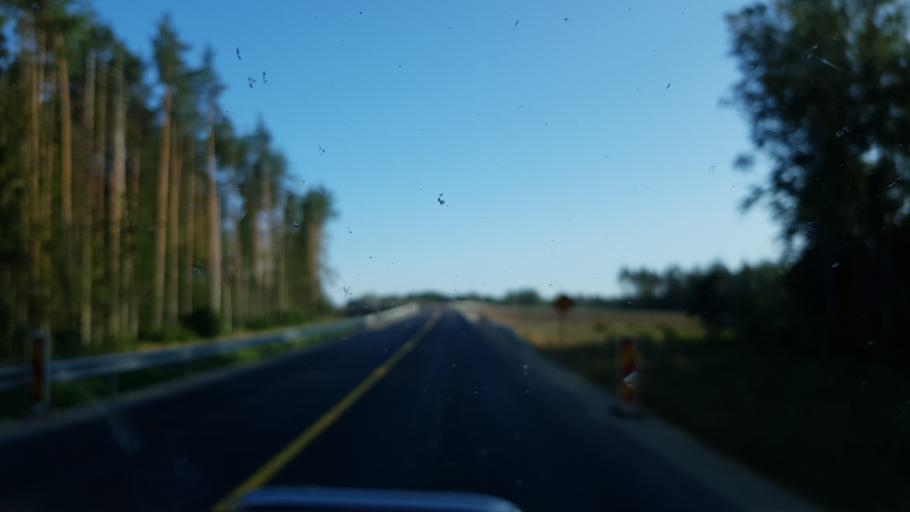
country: EE
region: Harju
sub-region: Raasiku vald
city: Raasiku
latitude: 59.1617
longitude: 25.1901
